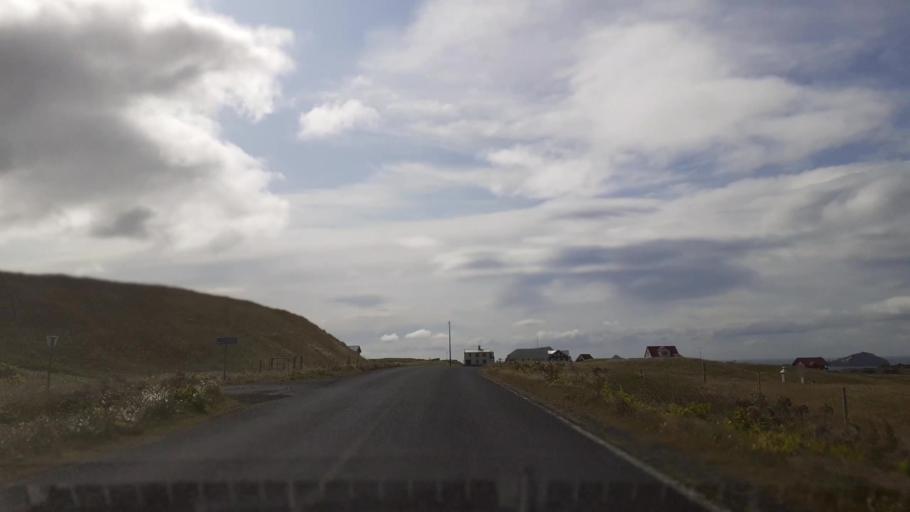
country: IS
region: South
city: Vestmannaeyjar
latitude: 63.4275
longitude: -20.2886
